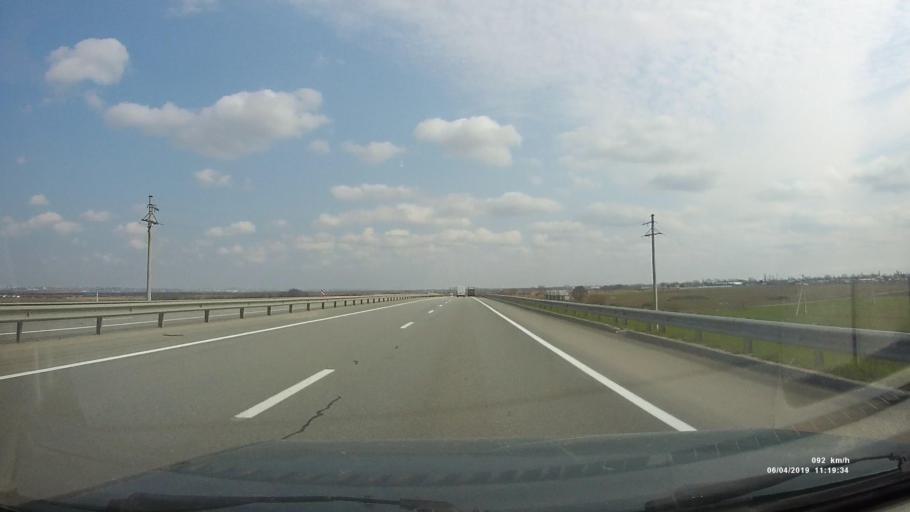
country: RU
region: Rostov
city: Kuleshovka
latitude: 47.1063
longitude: 39.6234
